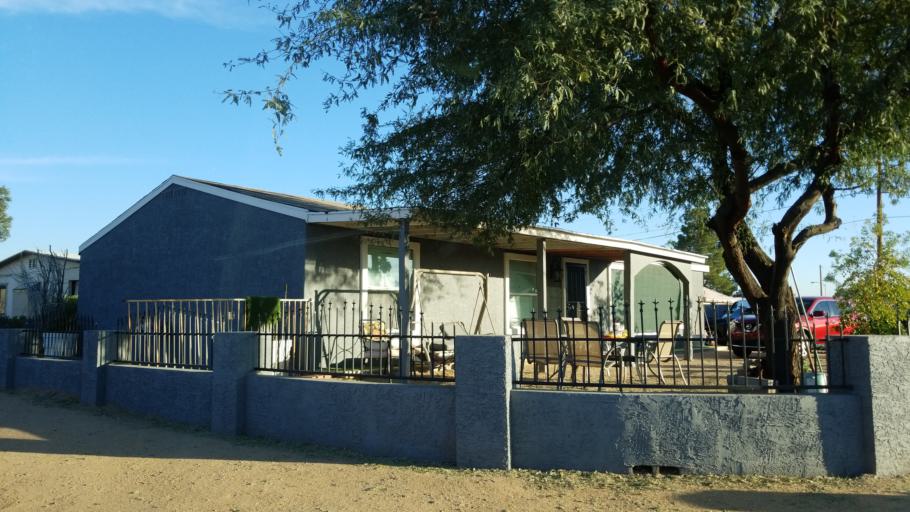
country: US
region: Arizona
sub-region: Maricopa County
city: Paradise Valley
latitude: 33.6512
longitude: -112.0361
